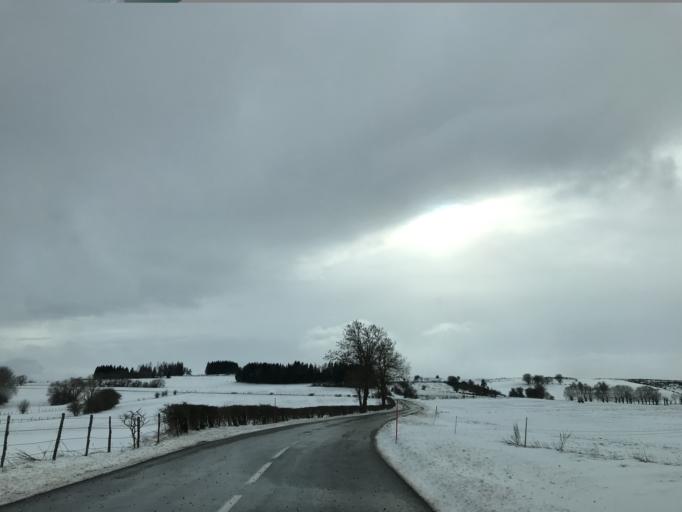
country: FR
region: Auvergne
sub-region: Departement du Puy-de-Dome
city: Aydat
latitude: 45.6789
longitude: 2.9354
